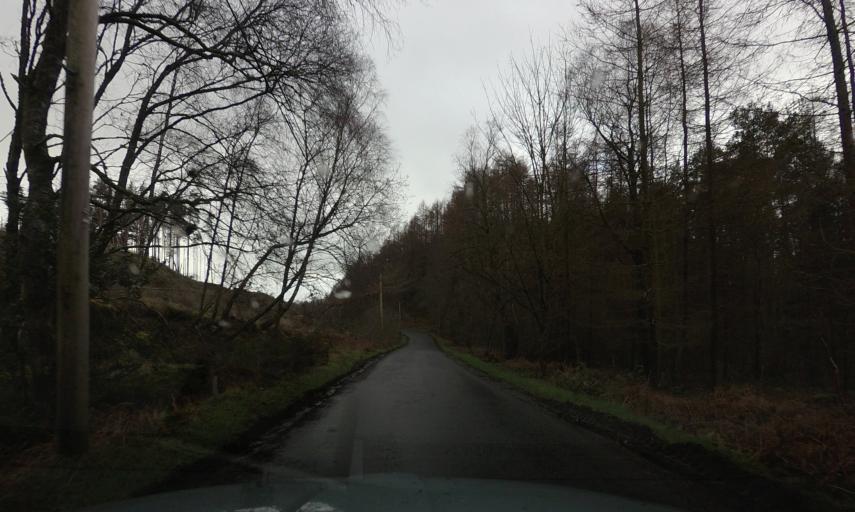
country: GB
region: Scotland
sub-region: West Dunbartonshire
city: Balloch
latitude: 56.1475
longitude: -4.6390
